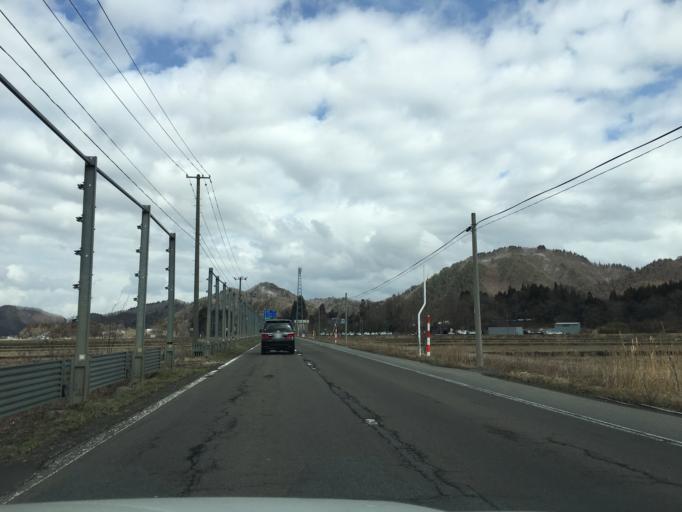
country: JP
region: Akita
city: Hanawa
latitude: 40.2269
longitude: 140.7280
